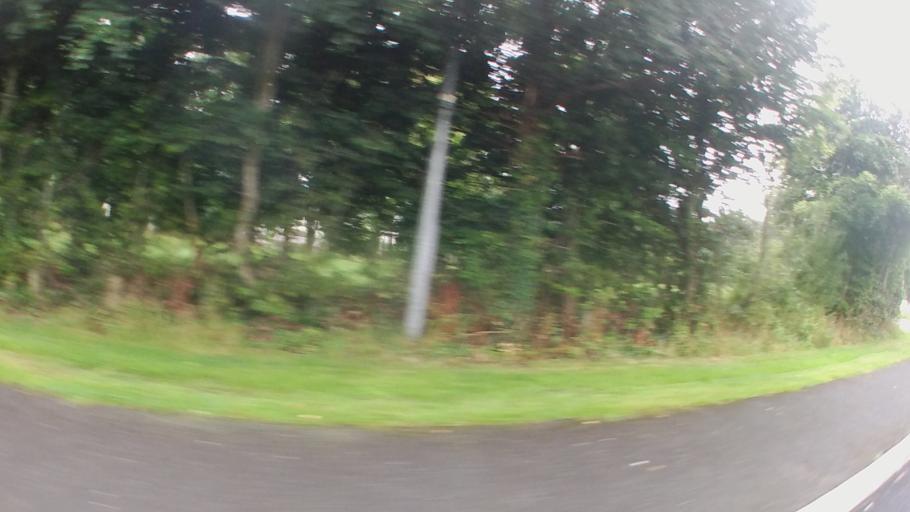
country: IE
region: Leinster
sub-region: Kilkenny
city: Callan
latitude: 52.5534
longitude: -7.3811
